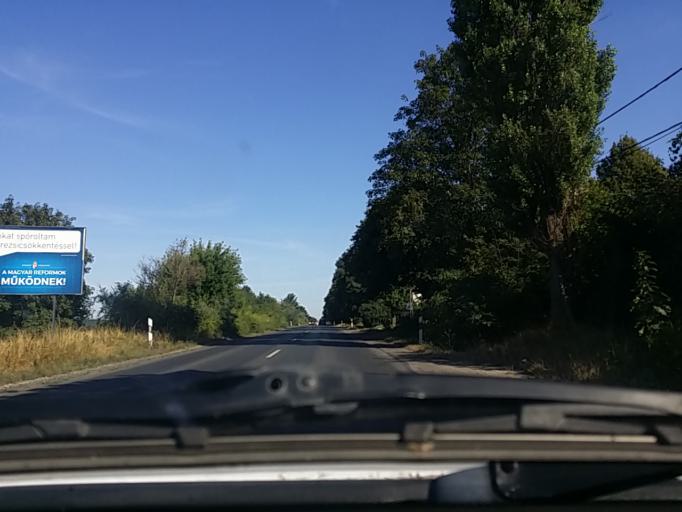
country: HU
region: Pest
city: Solymar
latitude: 47.6110
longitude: 18.9351
